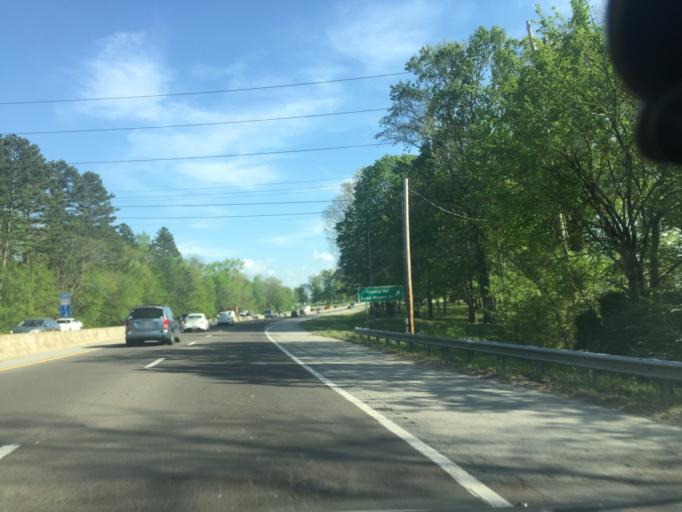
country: US
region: Tennessee
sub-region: Hamilton County
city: East Chattanooga
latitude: 35.1145
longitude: -85.2309
